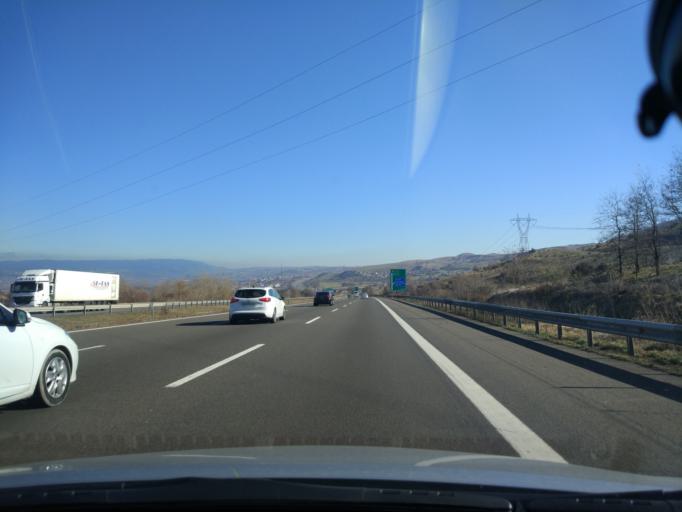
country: TR
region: Bolu
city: Yenicaga
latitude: 40.7618
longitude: 31.9904
